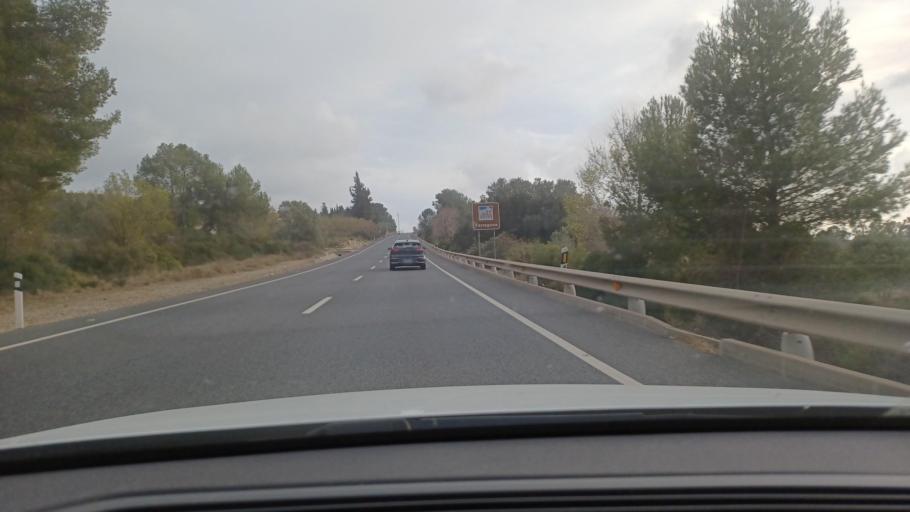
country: ES
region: Catalonia
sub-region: Provincia de Tarragona
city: els Pallaresos
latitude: 41.1677
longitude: 1.2397
